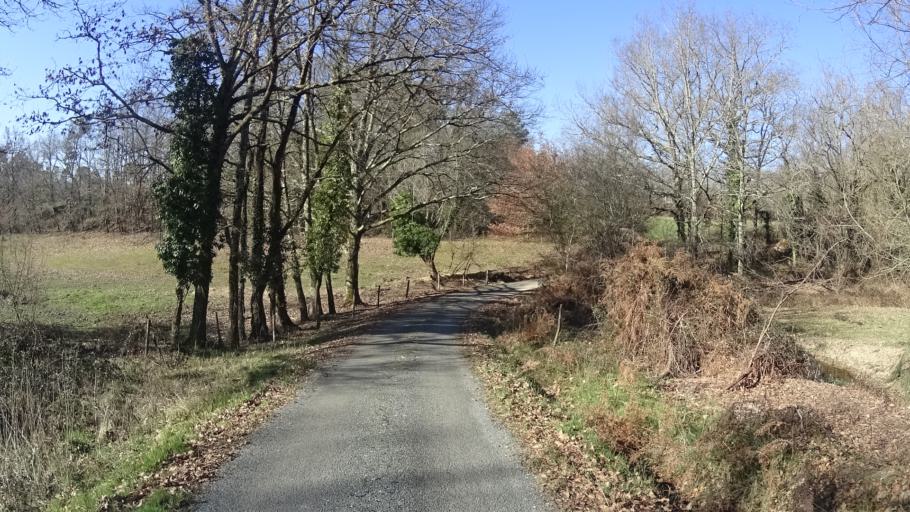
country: FR
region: Aquitaine
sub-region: Departement de la Dordogne
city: Montpon-Menesterol
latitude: 45.0459
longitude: 0.2451
